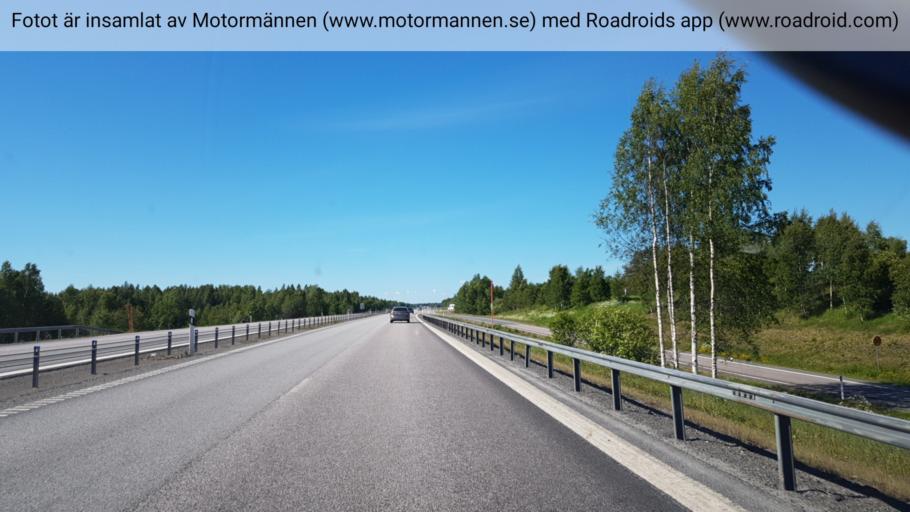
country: SE
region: Norrbotten
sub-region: Lulea Kommun
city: Sodra Sunderbyn
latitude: 65.5486
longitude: 21.8469
